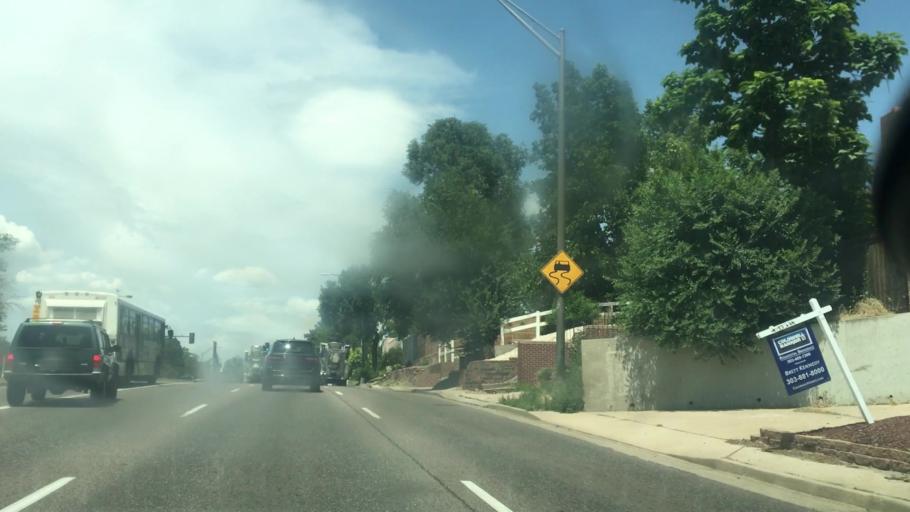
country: US
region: Colorado
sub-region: Arapahoe County
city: Glendale
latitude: 39.7168
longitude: -104.9406
